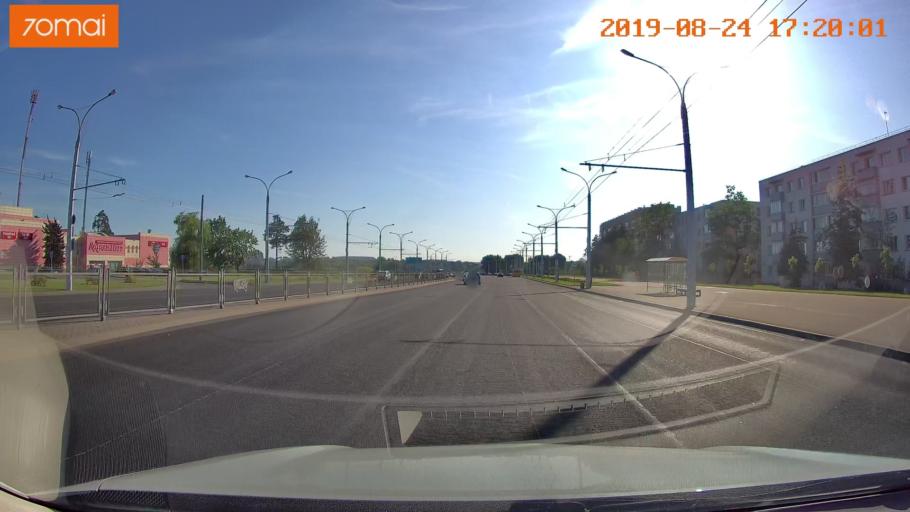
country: BY
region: Minsk
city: Hatava
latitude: 53.8573
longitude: 27.6392
